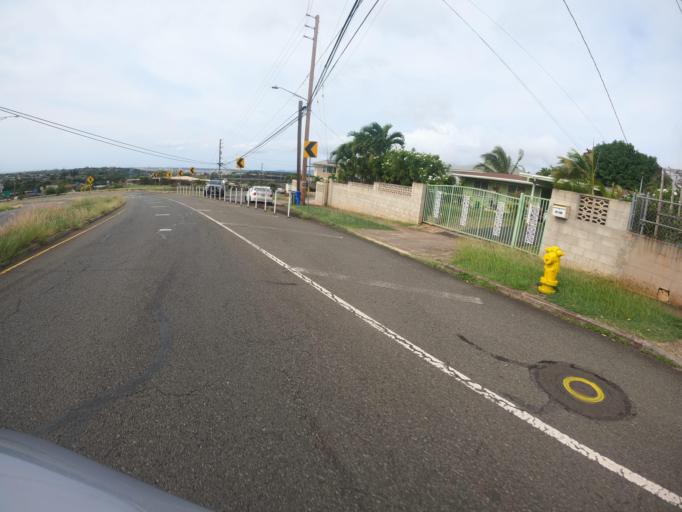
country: US
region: Hawaii
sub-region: Honolulu County
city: Halawa
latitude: 21.3749
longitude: -157.9188
